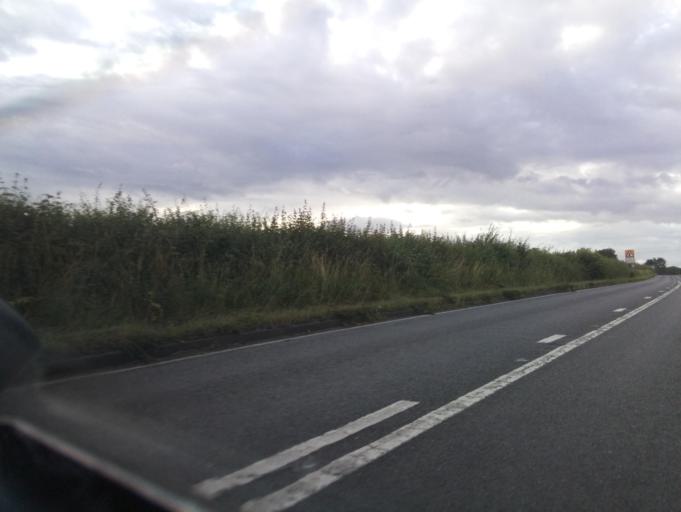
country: GB
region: England
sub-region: Oxfordshire
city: Kidlington
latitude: 51.8482
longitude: -1.3126
